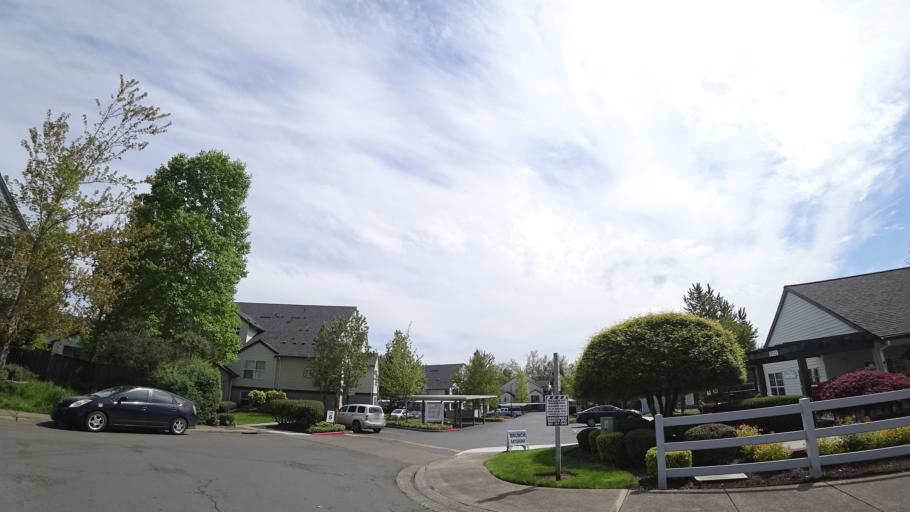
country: US
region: Oregon
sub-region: Washington County
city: Aloha
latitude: 45.4875
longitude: -122.8918
